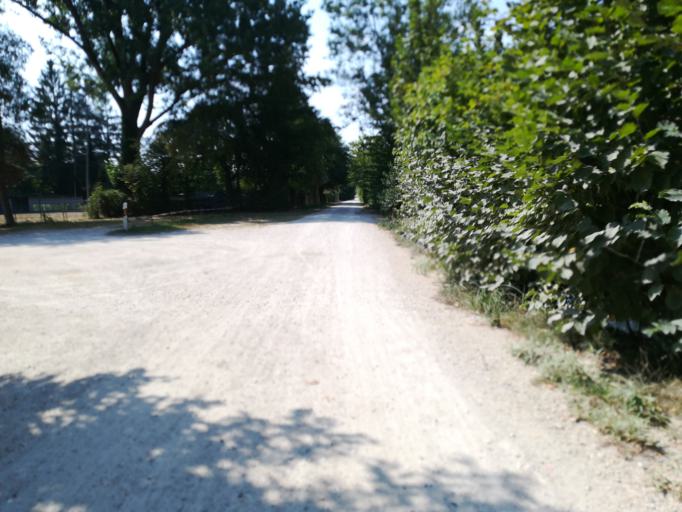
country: DE
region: Baden-Wuerttemberg
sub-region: Freiburg Region
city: Singen
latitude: 47.7803
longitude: 8.8332
